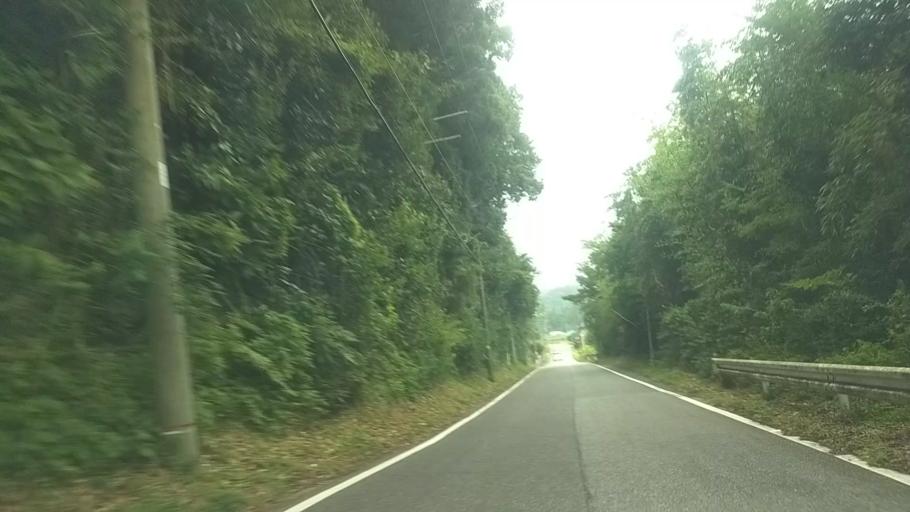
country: JP
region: Chiba
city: Kawaguchi
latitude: 35.2274
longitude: 140.0169
